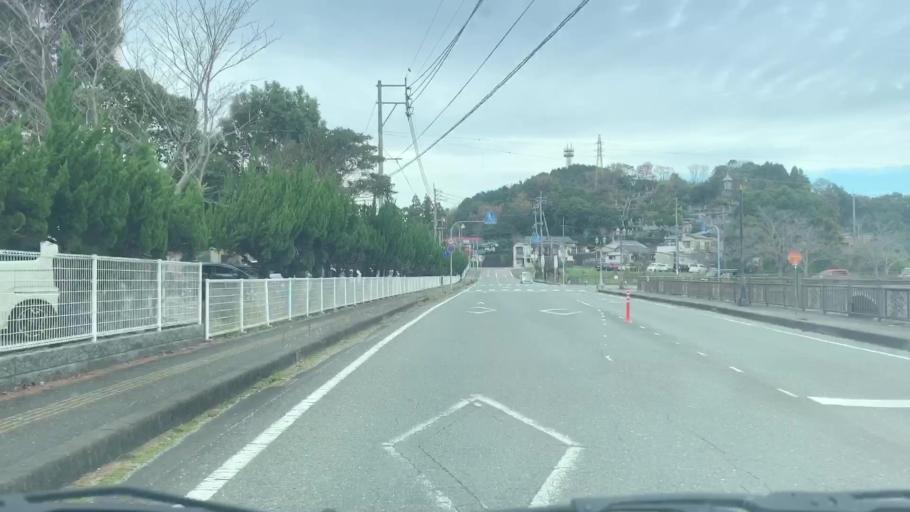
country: JP
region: Saga Prefecture
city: Ureshinomachi-shimojuku
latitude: 33.0984
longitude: 129.9802
